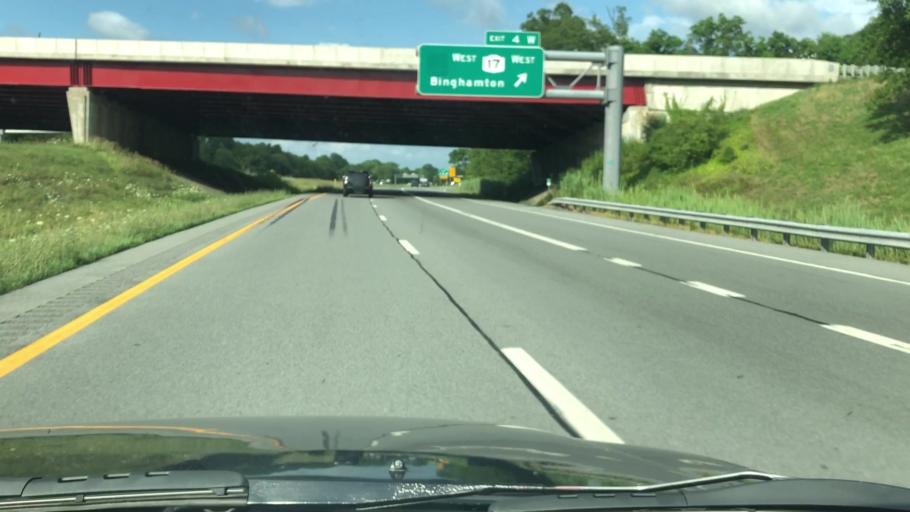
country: US
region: New York
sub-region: Orange County
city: Mechanicstown
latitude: 41.4470
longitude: -74.3703
